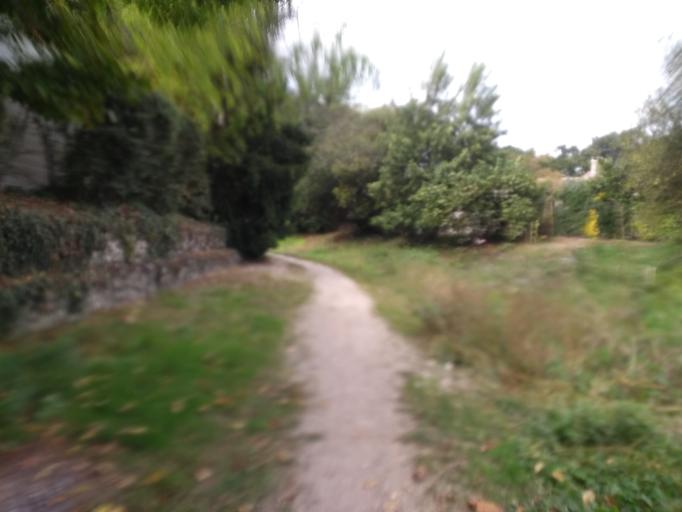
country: FR
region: Aquitaine
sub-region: Departement de la Gironde
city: Pessac
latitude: 44.8137
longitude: -0.6437
